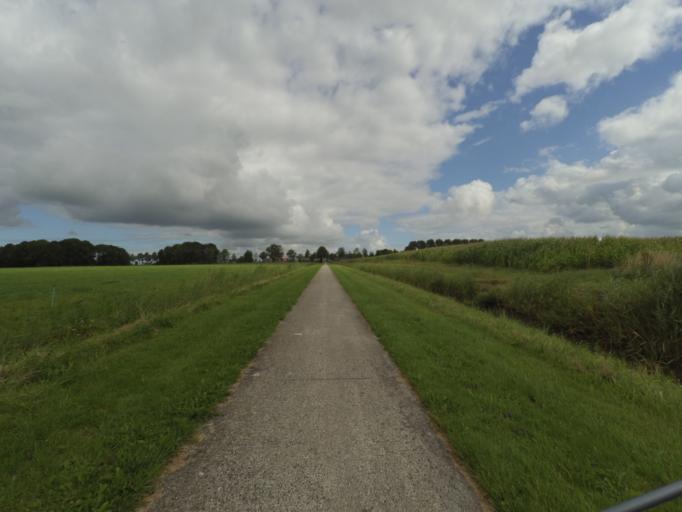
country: NL
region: Friesland
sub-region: Gemeente Kollumerland en Nieuwkruisland
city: Kollum
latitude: 53.2923
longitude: 6.2309
